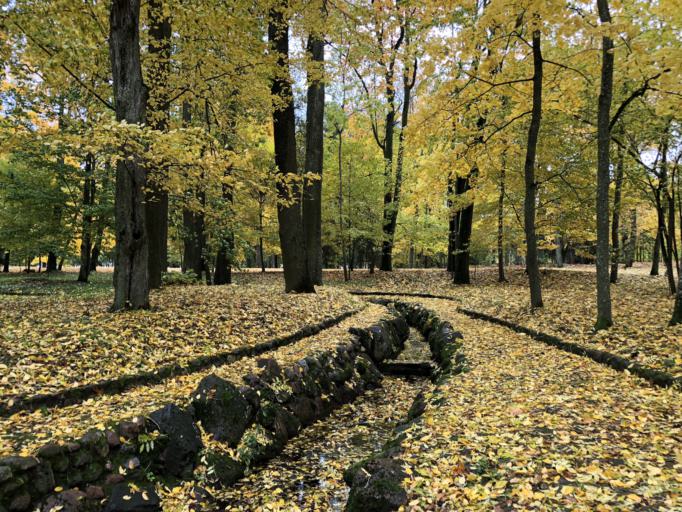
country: BY
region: Minsk
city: Nyasvizh
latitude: 53.2245
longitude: 26.6921
